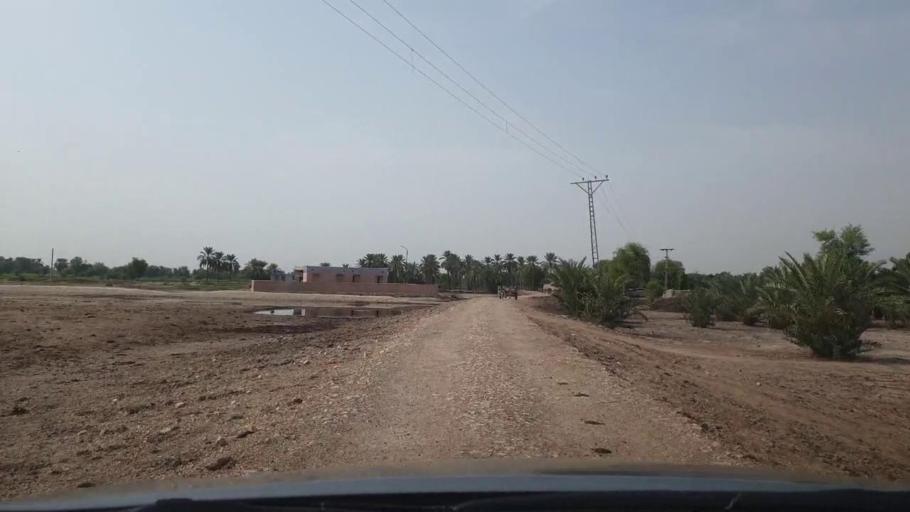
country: PK
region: Sindh
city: Rohri
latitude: 27.6614
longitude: 69.0132
